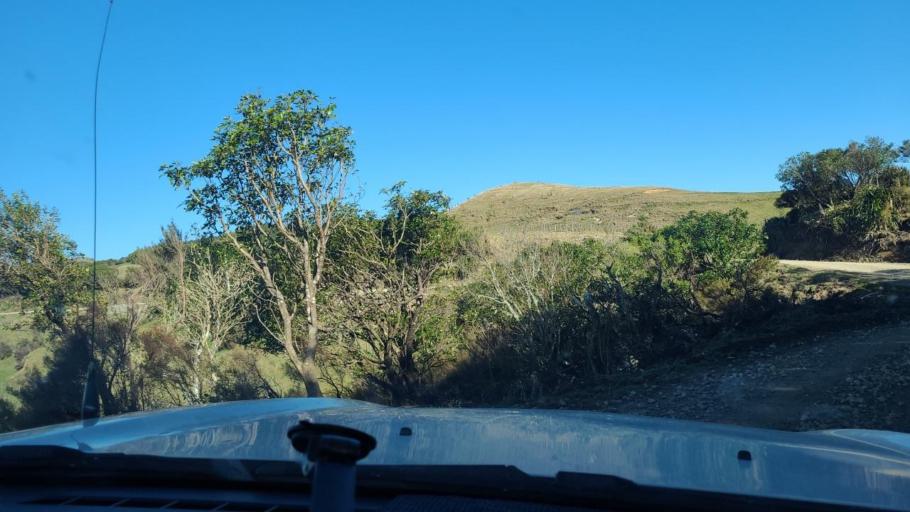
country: NZ
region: Hawke's Bay
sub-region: Wairoa District
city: Wairoa
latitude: -38.6807
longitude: 177.4645
